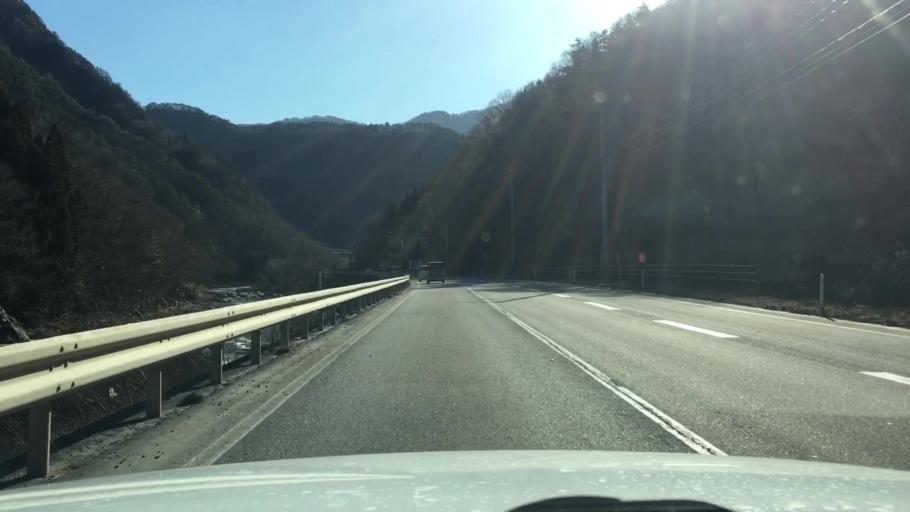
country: JP
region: Iwate
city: Miyako
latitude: 39.6145
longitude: 141.7886
